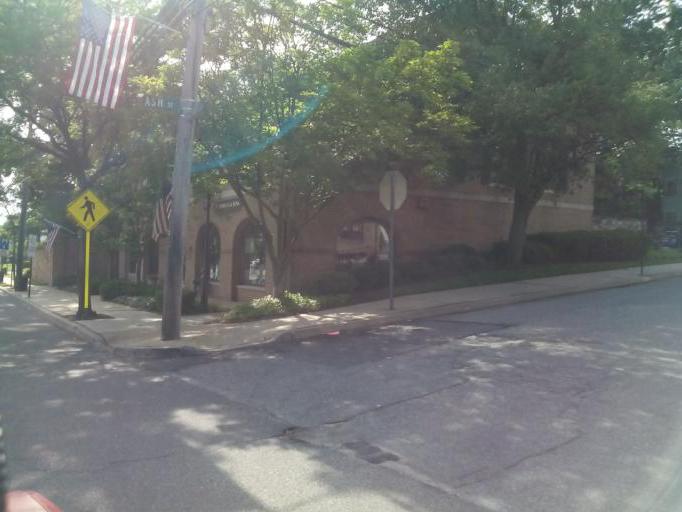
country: US
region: New York
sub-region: Nassau County
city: Locust Valley
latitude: 40.8757
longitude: -73.5992
